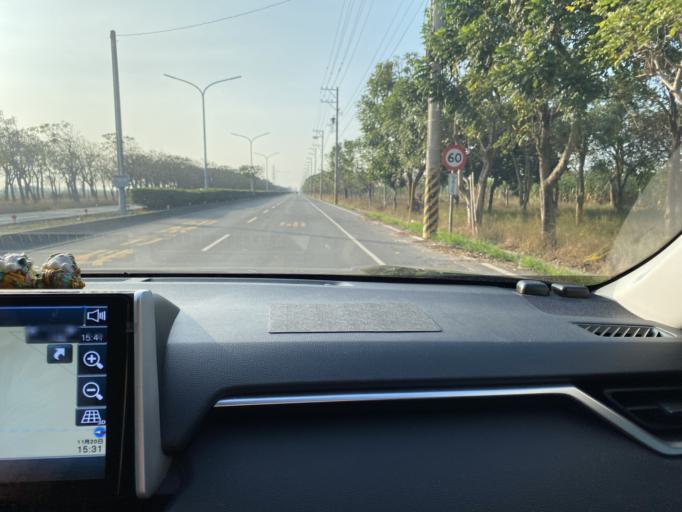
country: TW
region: Taiwan
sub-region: Changhua
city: Chang-hua
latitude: 23.9561
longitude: 120.4133
